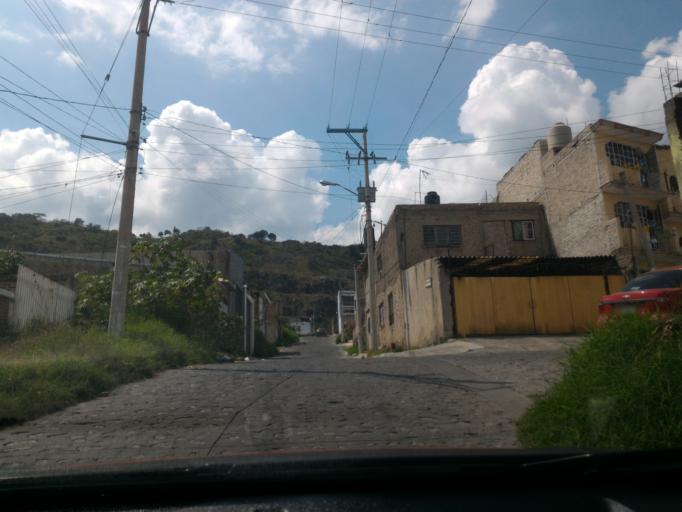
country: MX
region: Jalisco
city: Guadalajara
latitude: 20.6614
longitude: -103.4538
